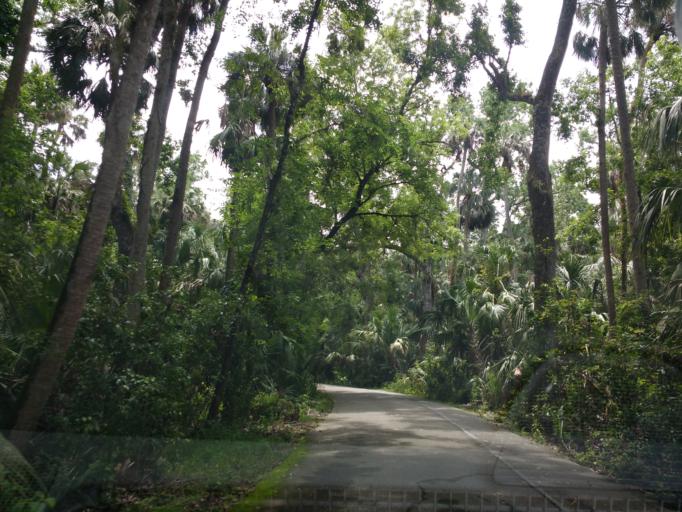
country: US
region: Florida
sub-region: Highlands County
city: Sebring
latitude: 27.4703
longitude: -81.5453
